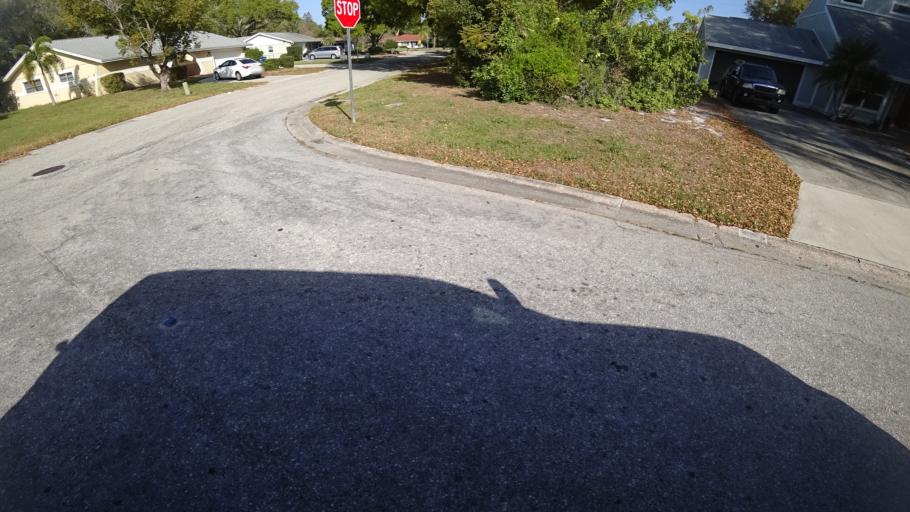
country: US
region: Florida
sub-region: Manatee County
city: Whitfield
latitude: 27.4125
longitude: -82.5635
